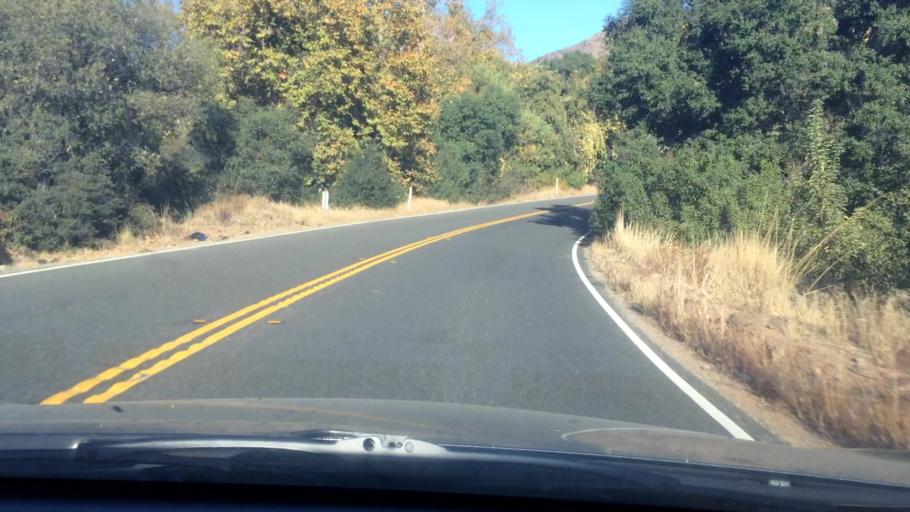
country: US
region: California
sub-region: Orange County
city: Coto De Caza
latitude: 33.5865
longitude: -117.5215
